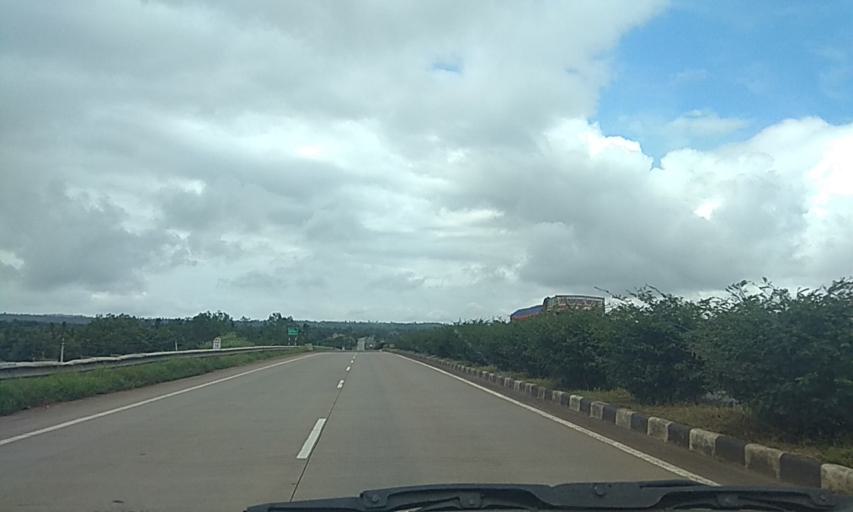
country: IN
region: Karnataka
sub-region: Belgaum
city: Sankeshwar
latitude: 16.3136
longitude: 74.4275
